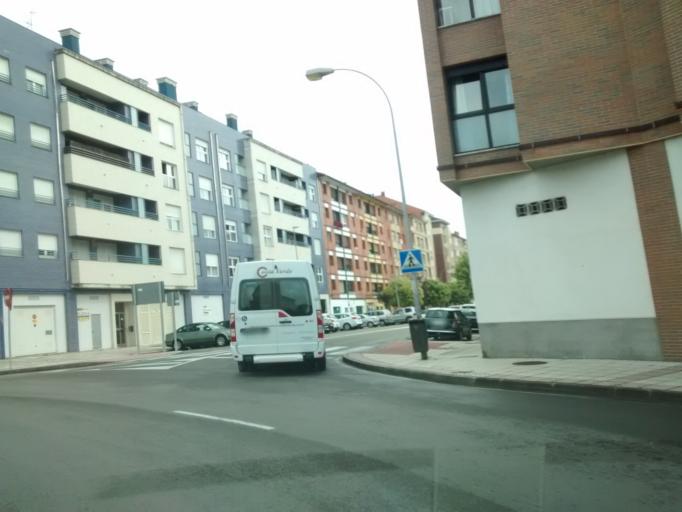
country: ES
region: Asturias
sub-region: Province of Asturias
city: Villaviciosa
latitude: 43.4785
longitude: -5.4391
